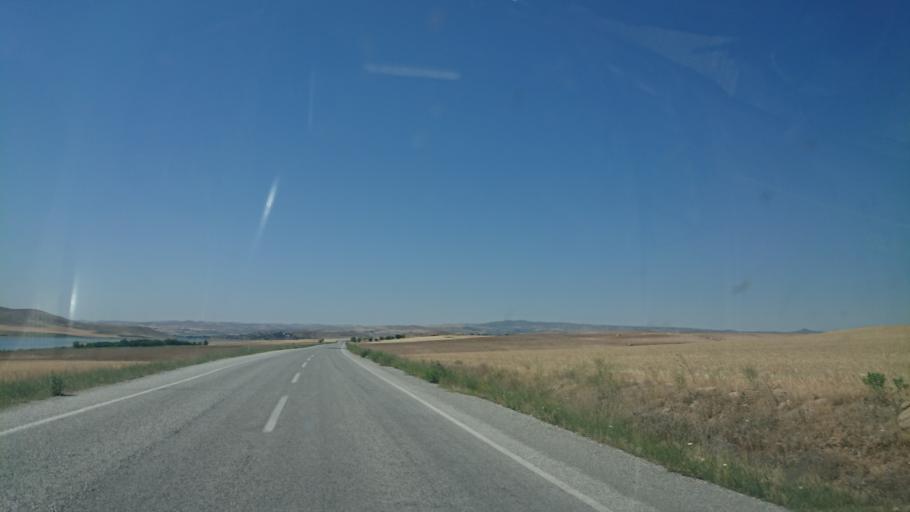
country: TR
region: Aksaray
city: Sariyahsi
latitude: 39.0546
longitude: 33.8979
